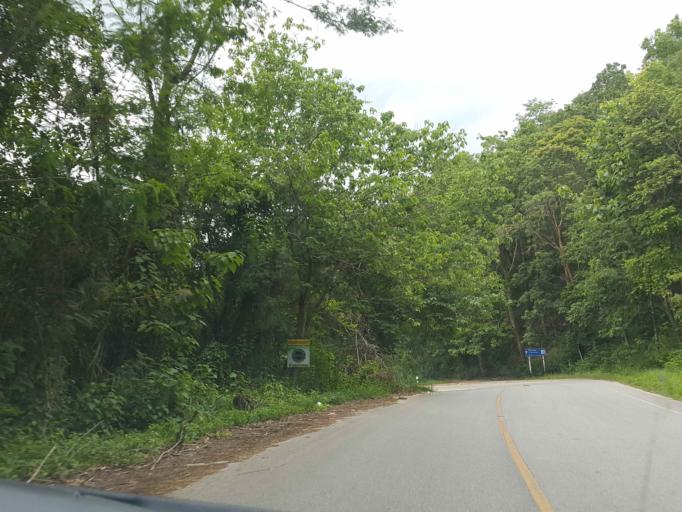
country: TH
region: Chiang Mai
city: Hang Dong
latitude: 18.7789
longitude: 98.8530
